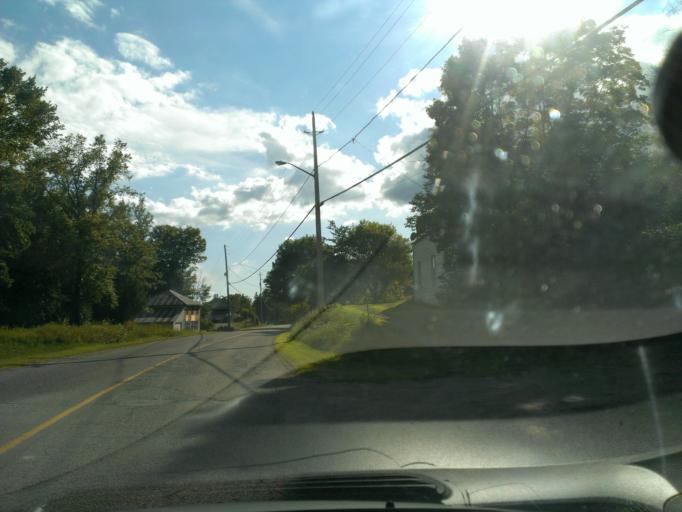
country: CA
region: Ontario
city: Skatepark
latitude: 44.7245
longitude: -76.9232
